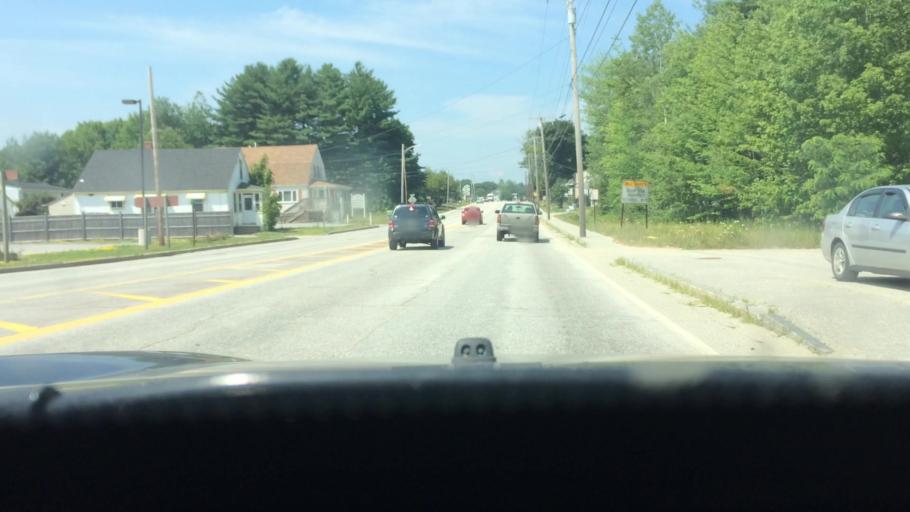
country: US
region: Maine
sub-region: Androscoggin County
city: Auburn
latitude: 44.0815
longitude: -70.2635
